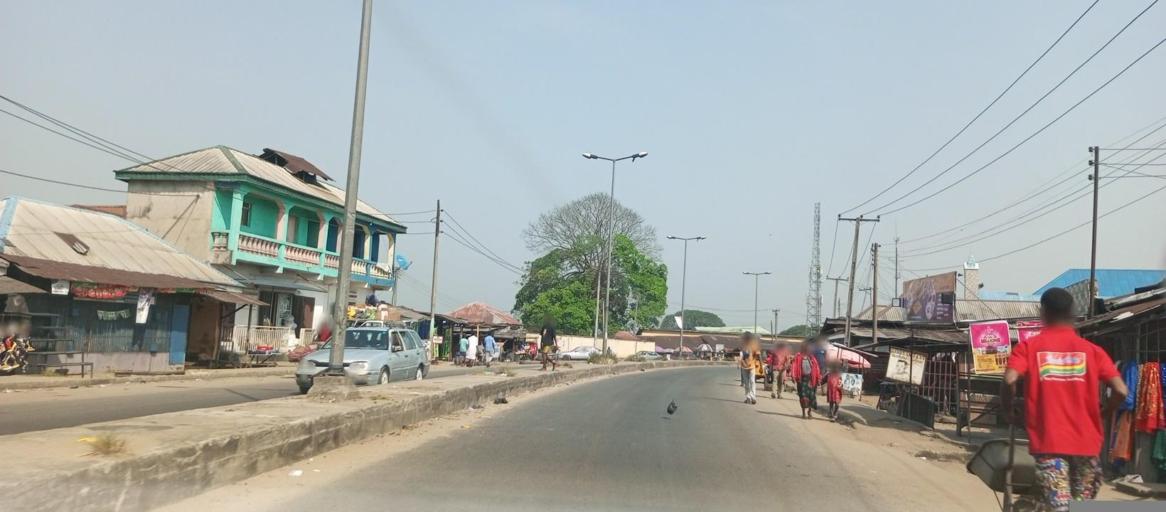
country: NG
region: Rivers
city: Emuoha
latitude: 4.8872
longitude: 6.9009
